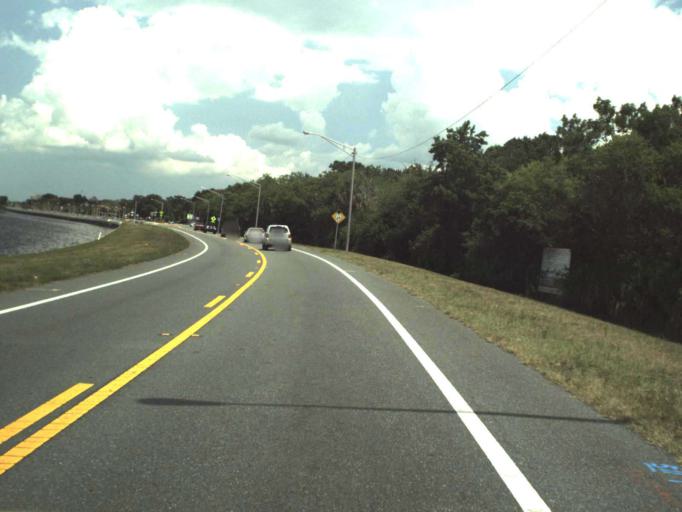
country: US
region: Florida
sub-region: Seminole County
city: Sanford
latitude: 28.8170
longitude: -81.2875
